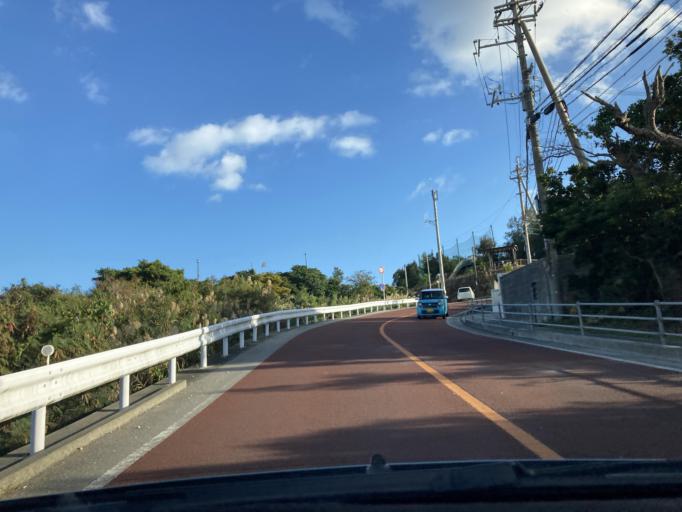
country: JP
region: Okinawa
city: Chatan
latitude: 26.2951
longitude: 127.7997
